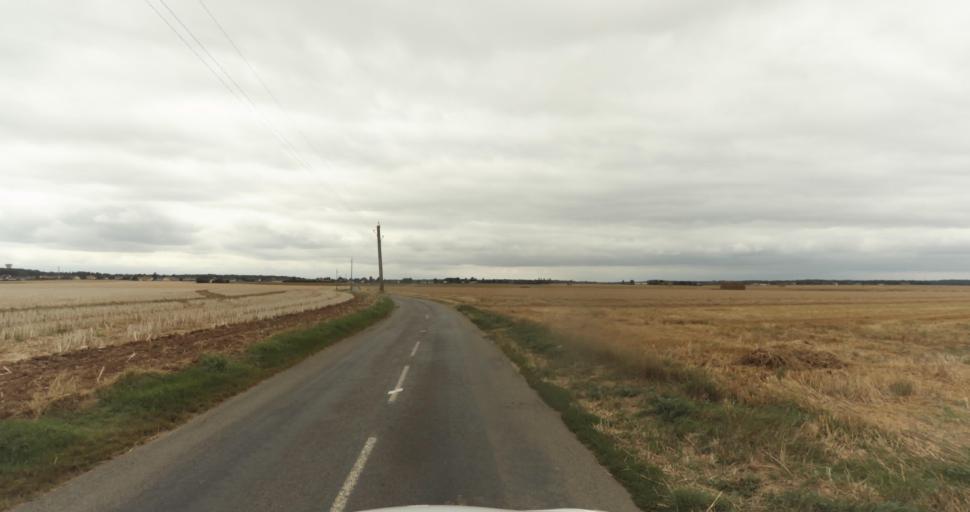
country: FR
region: Haute-Normandie
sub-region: Departement de l'Eure
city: Arnieres-sur-Iton
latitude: 48.9449
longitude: 1.1355
